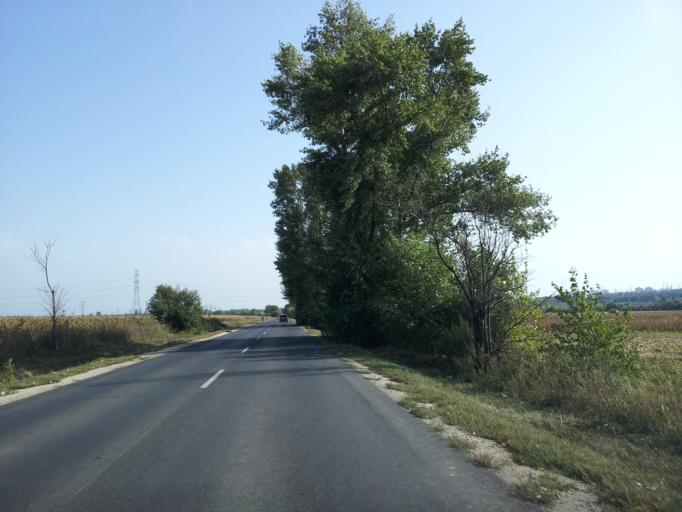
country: HU
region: Pest
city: Szazhalombatta
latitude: 47.3427
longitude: 18.9078
